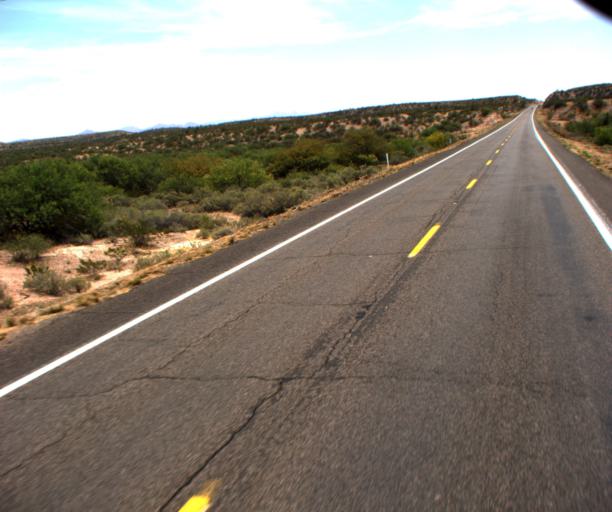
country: US
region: Arizona
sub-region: Graham County
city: Bylas
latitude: 33.2344
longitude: -110.2451
